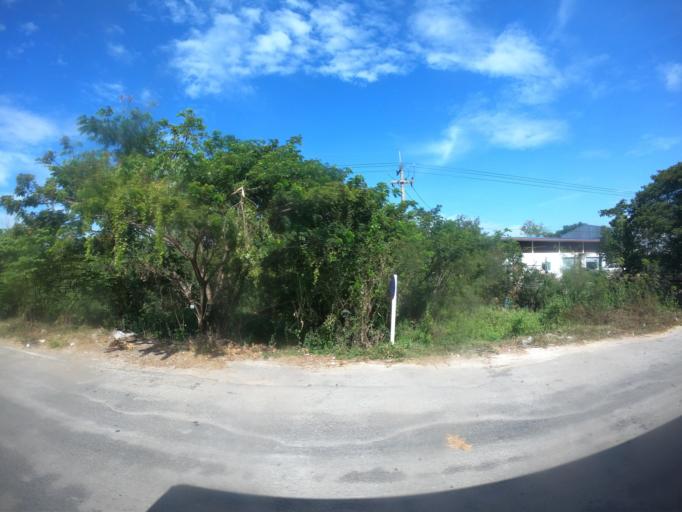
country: TH
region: Khon Kaen
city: Khon Kaen
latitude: 16.4124
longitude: 102.9029
